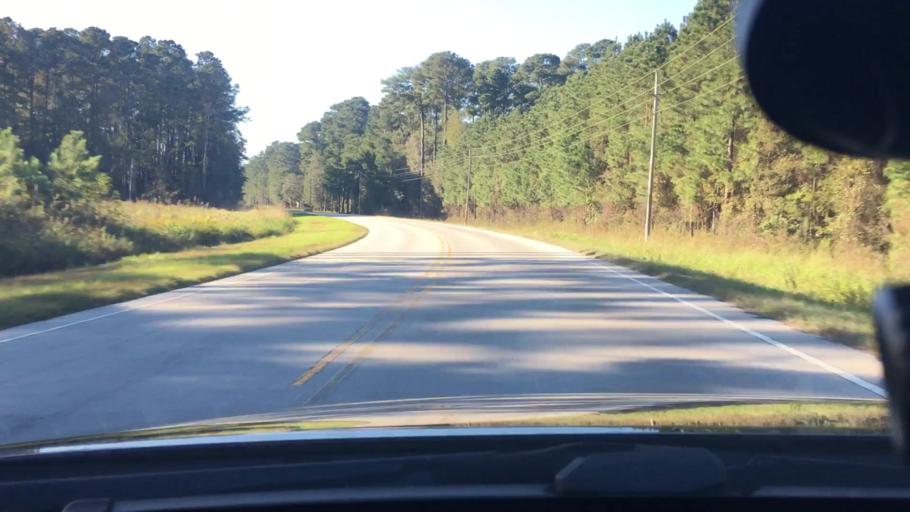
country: US
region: North Carolina
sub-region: Pitt County
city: Windsor
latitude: 35.4690
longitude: -77.2795
